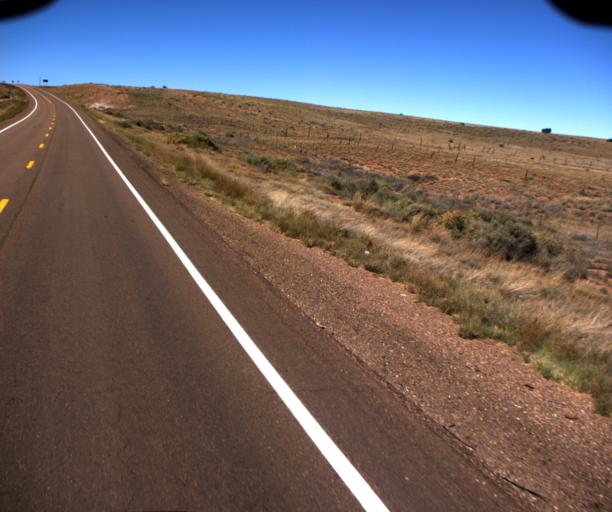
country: US
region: Arizona
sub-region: Apache County
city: Saint Johns
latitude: 34.5099
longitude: -109.4410
